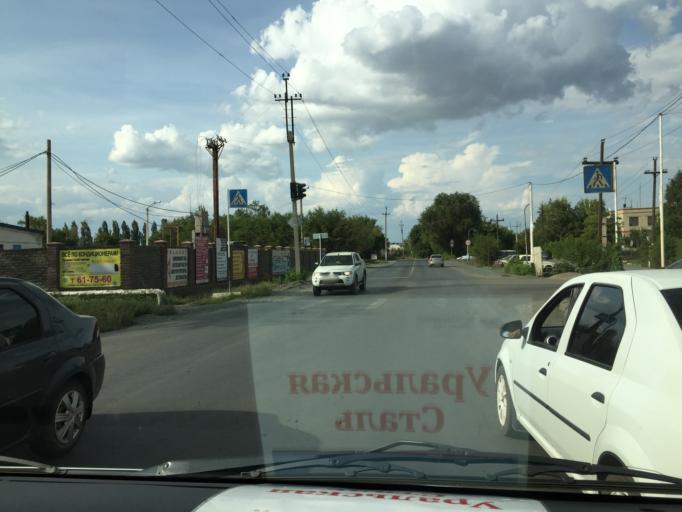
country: RU
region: Orenburg
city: Novotroitsk
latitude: 51.2108
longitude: 58.3072
